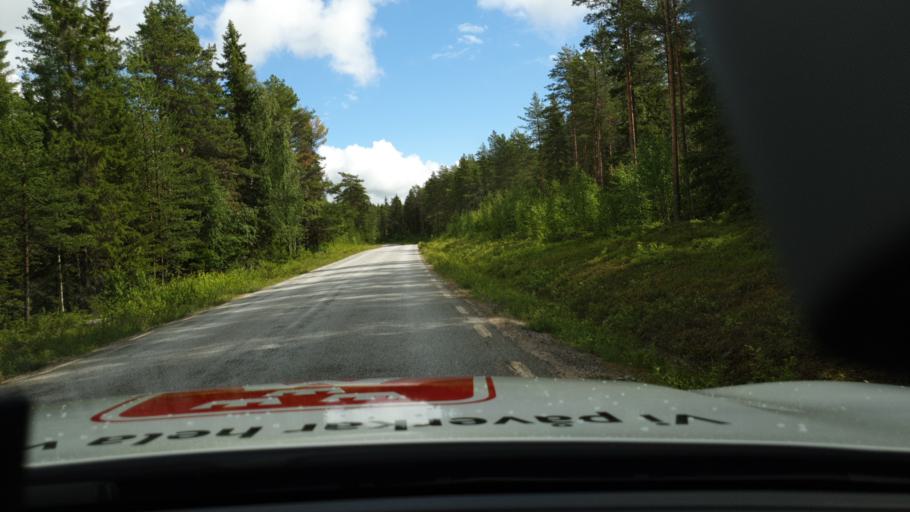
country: SE
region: Norrbotten
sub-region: Pitea Kommun
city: Rosvik
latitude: 65.4168
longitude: 21.7799
